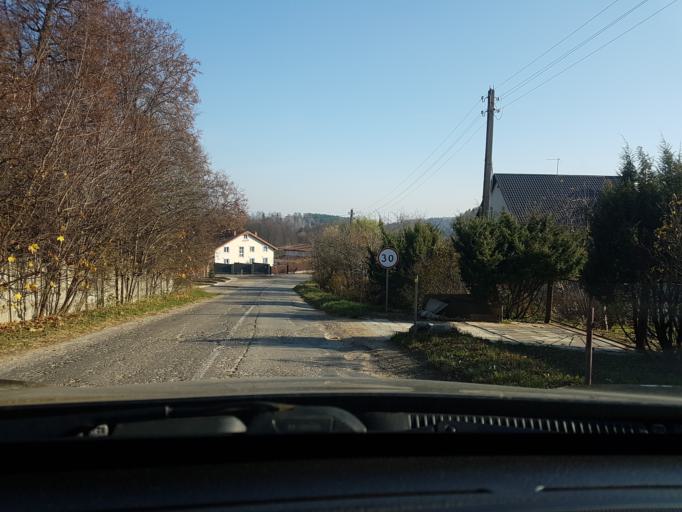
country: BY
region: Minsk
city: Azyartso
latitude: 53.8173
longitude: 27.3640
